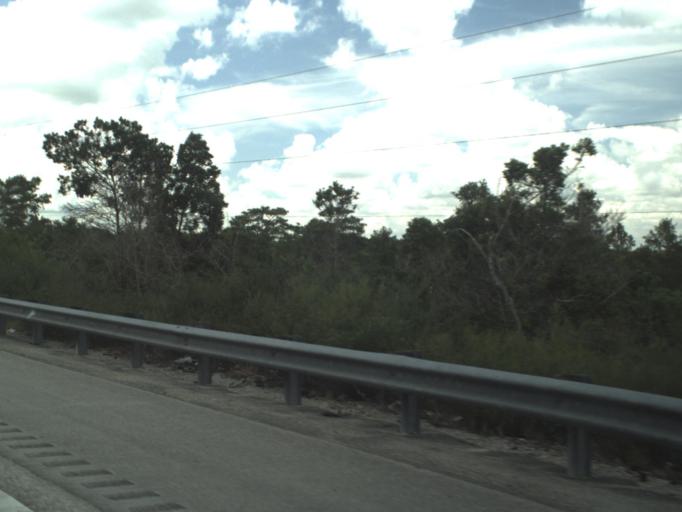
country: US
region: Florida
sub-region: Broward County
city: Weston
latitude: 26.1730
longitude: -80.8747
